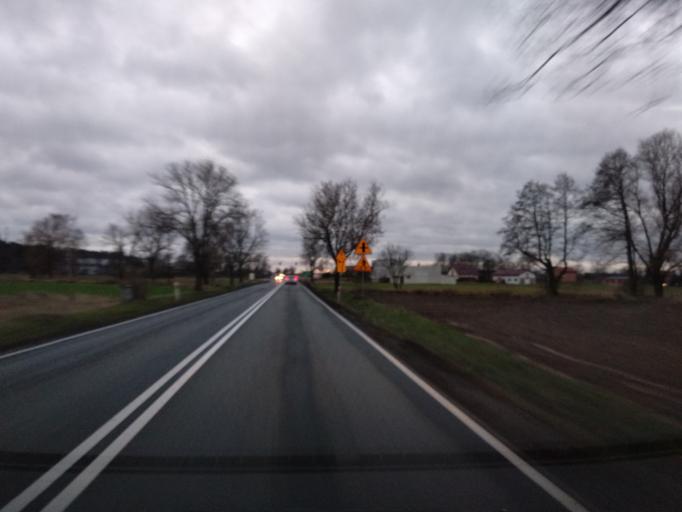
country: PL
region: Greater Poland Voivodeship
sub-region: Powiat koninski
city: Rychwal
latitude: 52.0978
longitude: 18.1673
